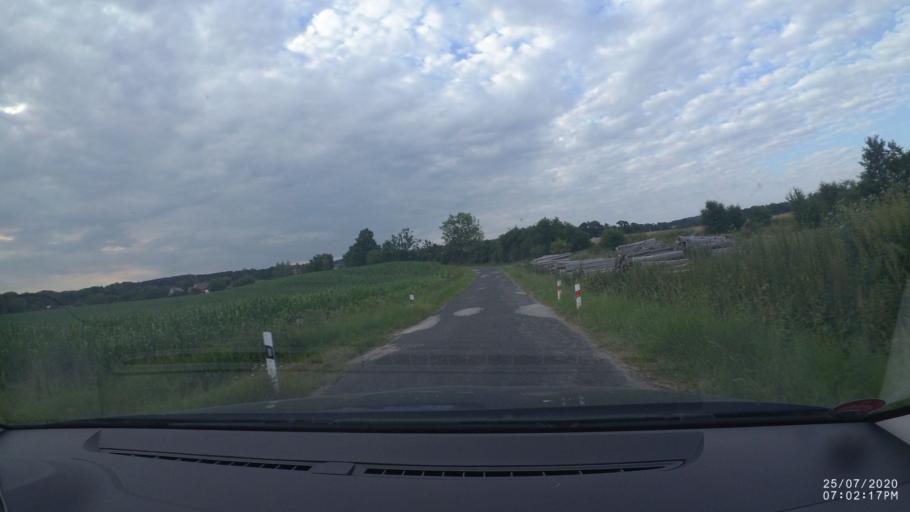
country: CZ
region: Kralovehradecky
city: Horice
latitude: 50.3546
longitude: 15.6726
